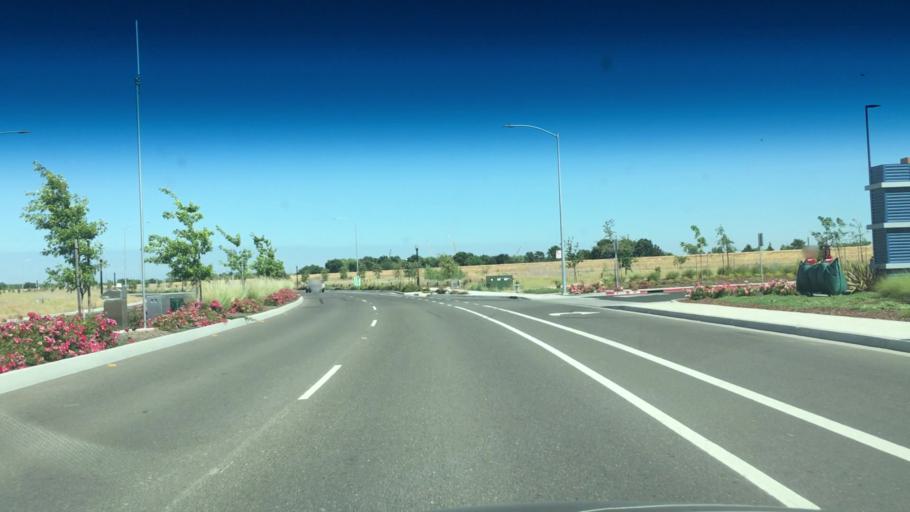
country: US
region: California
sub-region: Sacramento County
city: Parkway
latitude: 38.4593
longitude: -121.4886
